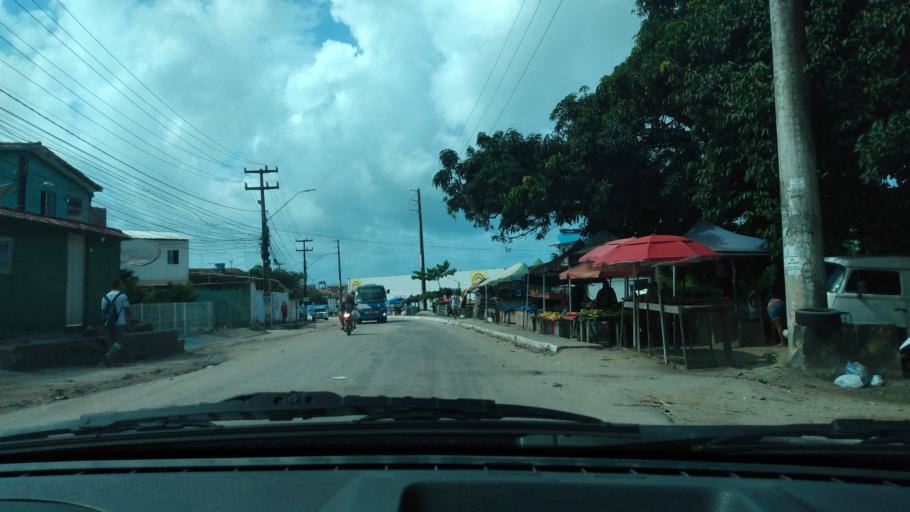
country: BR
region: Pernambuco
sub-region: Cabo De Santo Agostinho
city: Cabo
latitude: -8.3393
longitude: -34.9550
